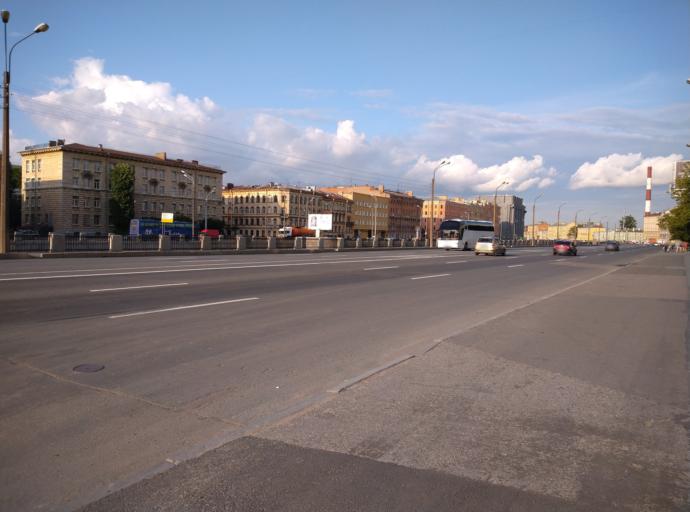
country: RU
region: St.-Petersburg
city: Admiralteisky
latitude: 59.9083
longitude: 30.3122
